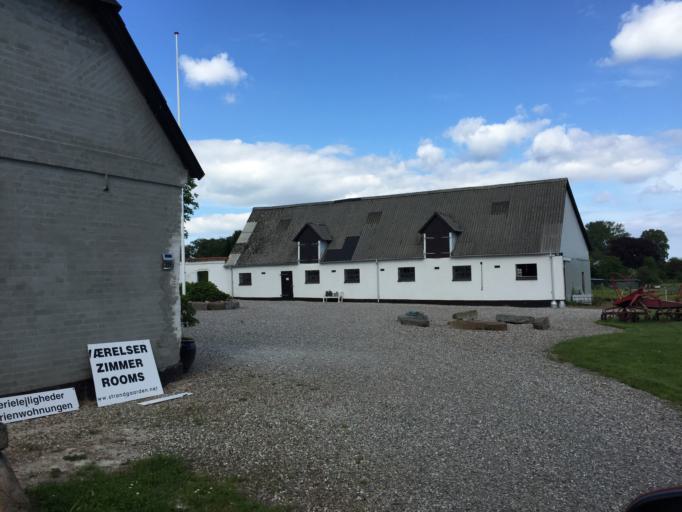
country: DK
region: South Denmark
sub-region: Aabenraa Kommune
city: Lojt Kirkeby
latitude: 55.1392
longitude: 9.4835
